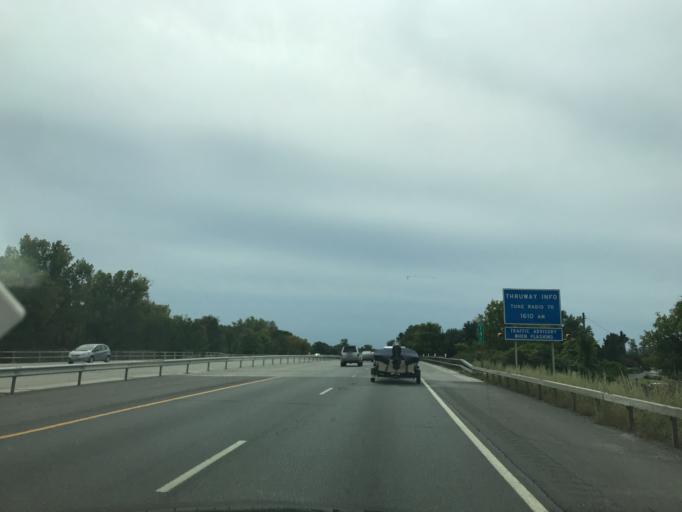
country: US
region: New York
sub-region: Albany County
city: Albany
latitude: 42.6212
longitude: -73.7805
